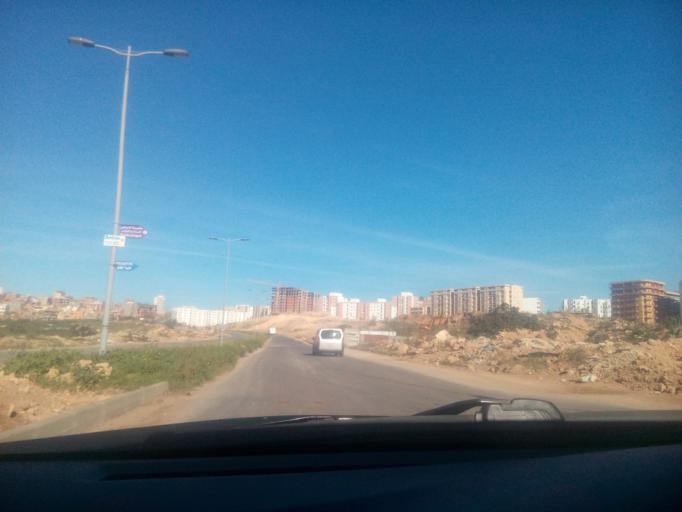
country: DZ
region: Oran
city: Bir el Djir
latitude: 35.7385
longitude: -0.5460
